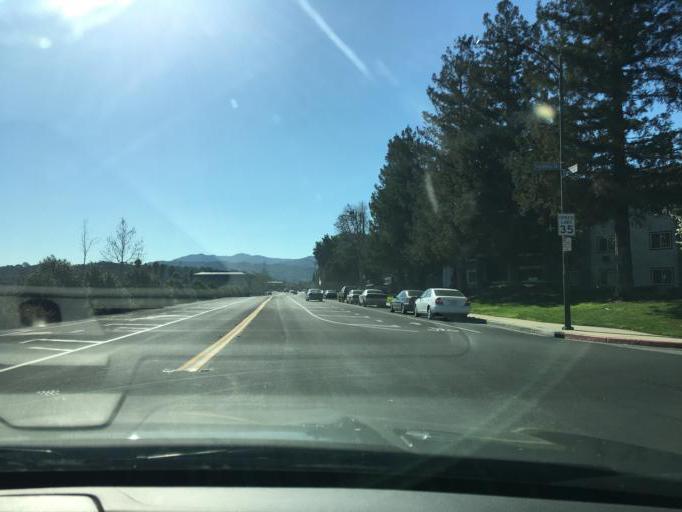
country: US
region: California
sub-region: Santa Clara County
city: Seven Trees
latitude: 37.2541
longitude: -121.8716
